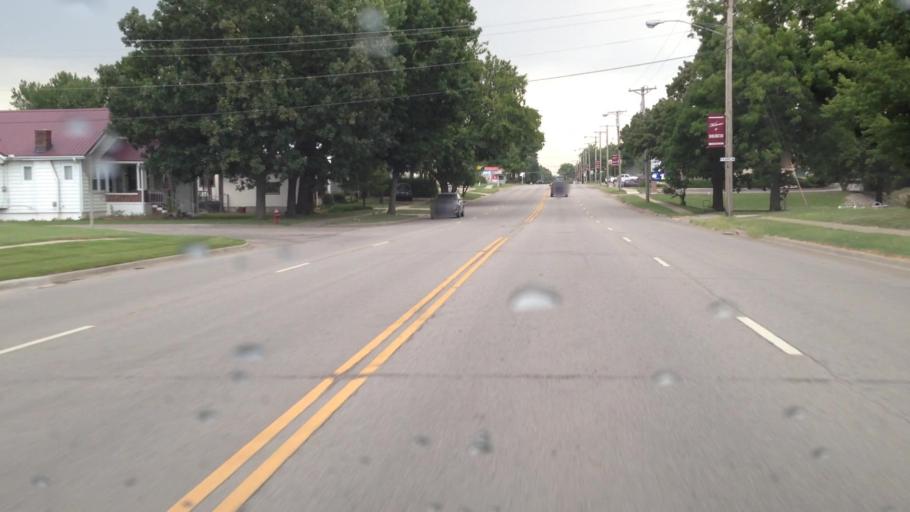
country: US
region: Kansas
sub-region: Coffey County
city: Burlington
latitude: 38.2008
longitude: -95.7386
